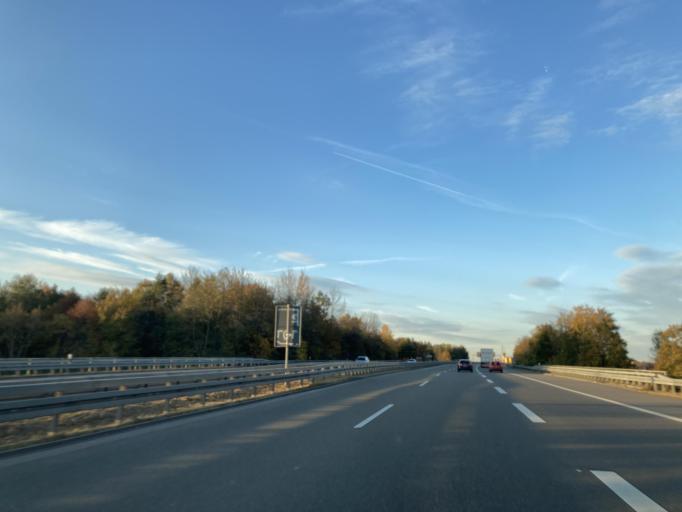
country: DE
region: Baden-Wuerttemberg
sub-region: Freiburg Region
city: Deisslingen
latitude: 48.0808
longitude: 8.5890
